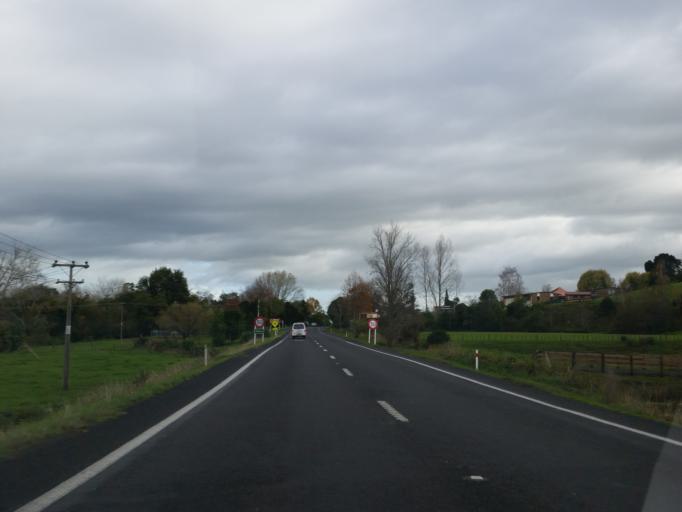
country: NZ
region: Waikato
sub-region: Hauraki District
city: Paeroa
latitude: -37.3877
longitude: 175.6813
